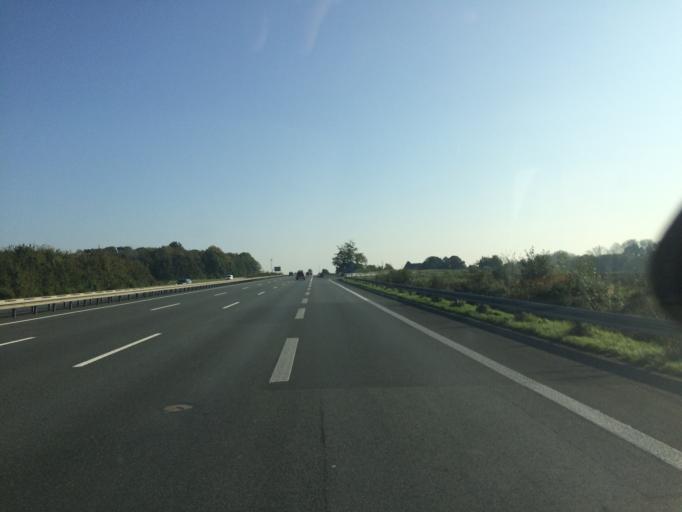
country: DE
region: North Rhine-Westphalia
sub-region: Regierungsbezirk Munster
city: Beckum
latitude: 51.7778
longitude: 8.0267
